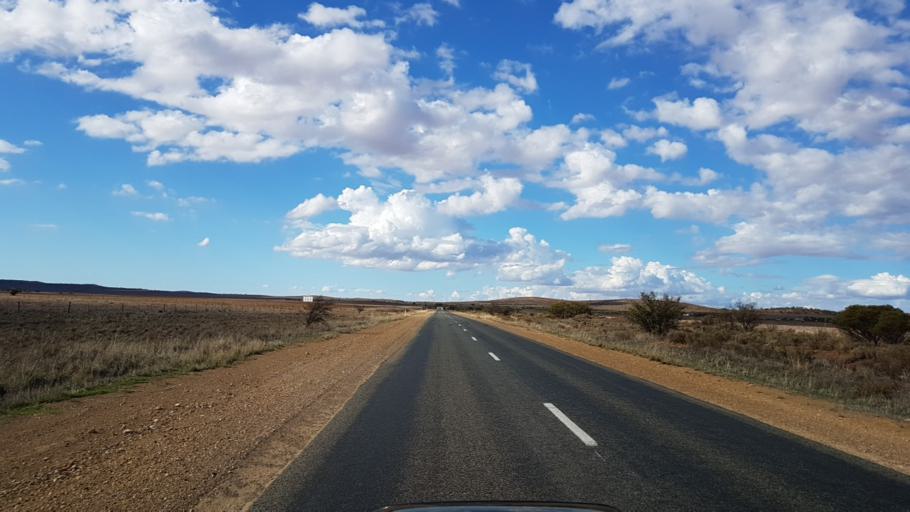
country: AU
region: South Australia
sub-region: Peterborough
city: Peterborough
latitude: -32.9670
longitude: 138.8731
